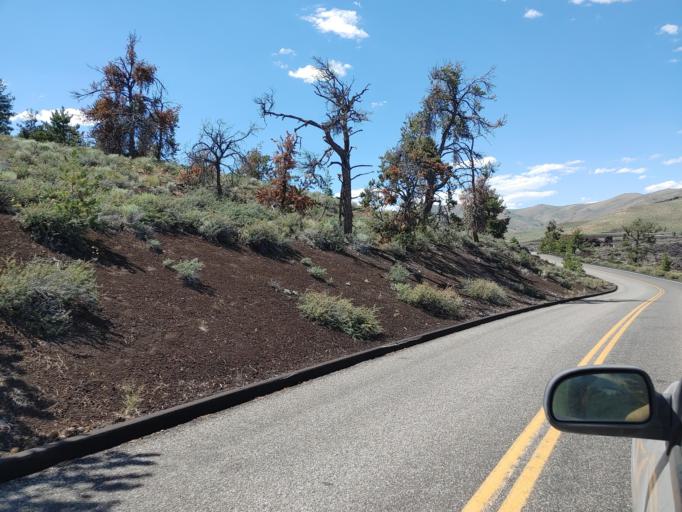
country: US
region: Idaho
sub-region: Butte County
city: Arco
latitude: 43.4547
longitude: -113.5573
